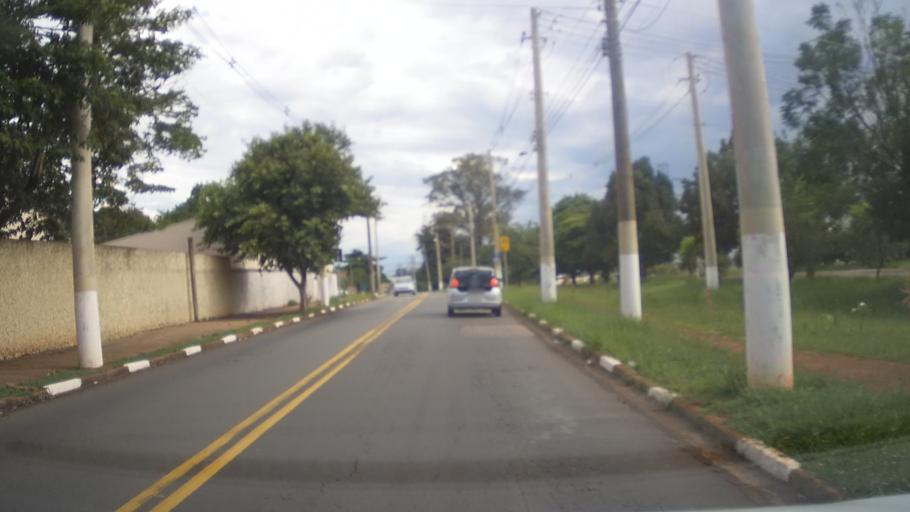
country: BR
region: Sao Paulo
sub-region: Campinas
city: Campinas
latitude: -22.8924
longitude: -47.1235
